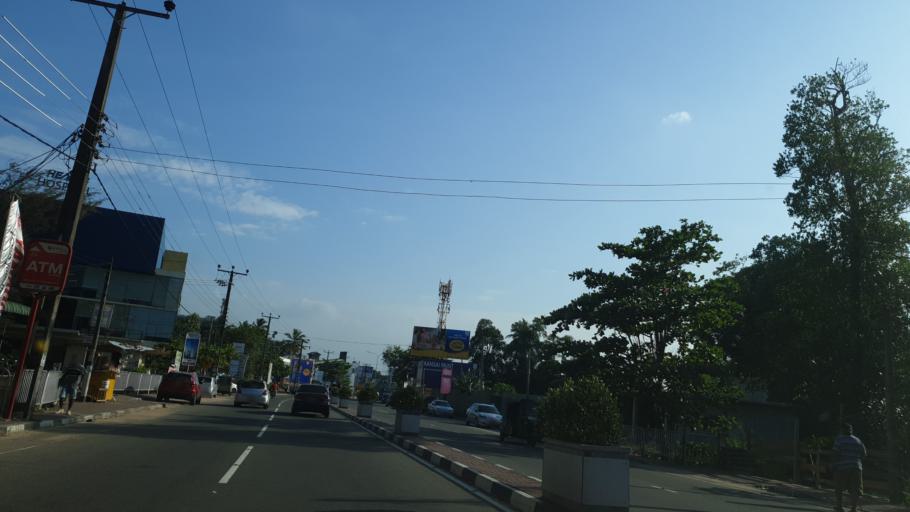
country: LK
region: Western
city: Battaramulla South
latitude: 6.8792
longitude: 79.9348
